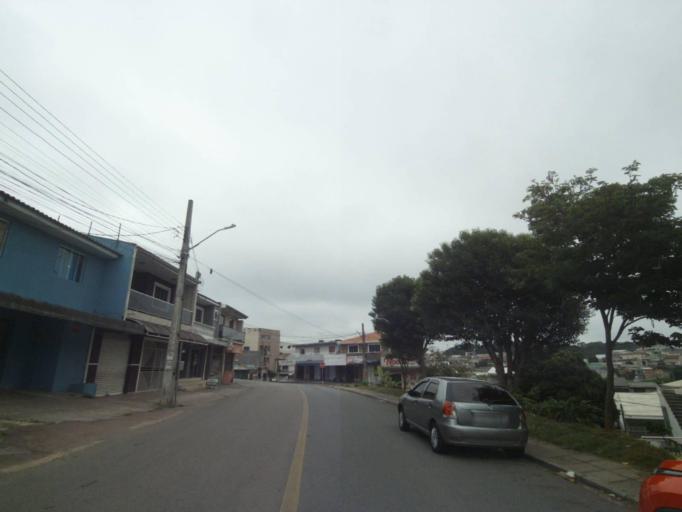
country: BR
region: Parana
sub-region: Curitiba
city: Curitiba
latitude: -25.4996
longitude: -49.3470
